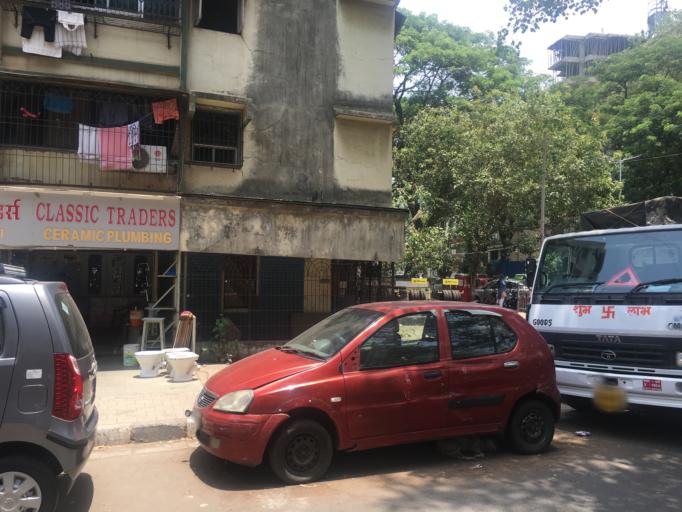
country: IN
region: Maharashtra
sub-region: Thane
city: Thane
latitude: 19.1663
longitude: 72.9597
